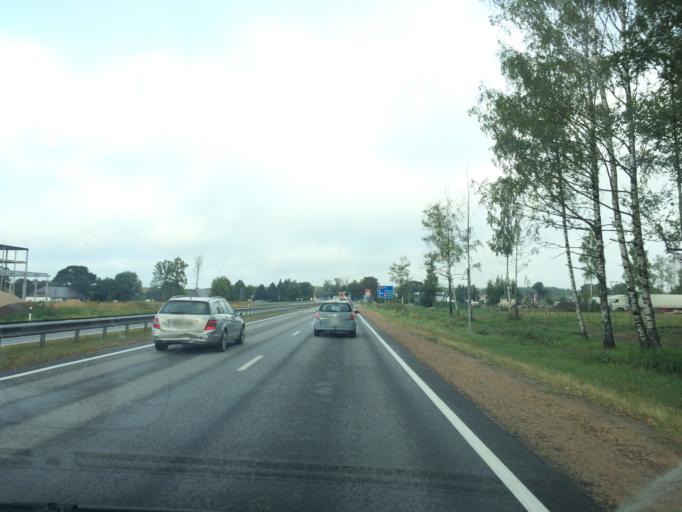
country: LV
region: Salaspils
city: Salaspils
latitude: 56.8546
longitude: 24.3260
